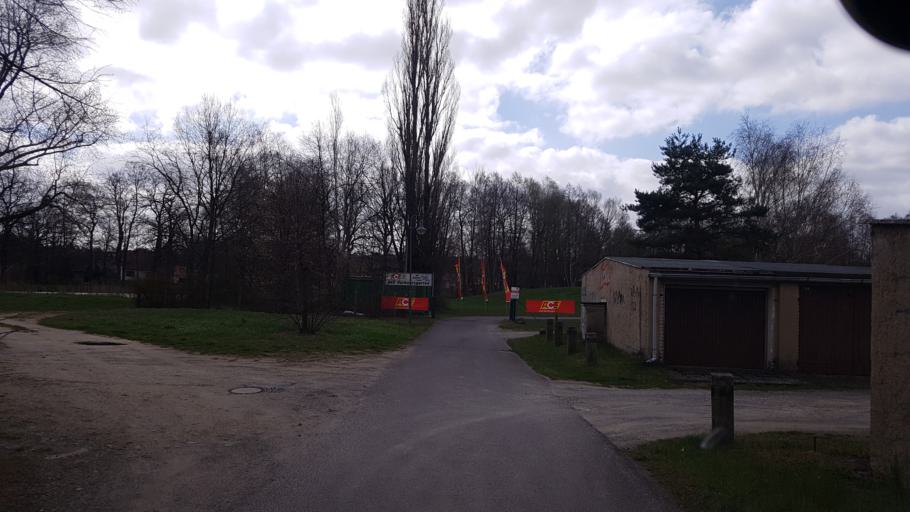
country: DE
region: Brandenburg
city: Calau
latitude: 51.7437
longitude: 13.9725
